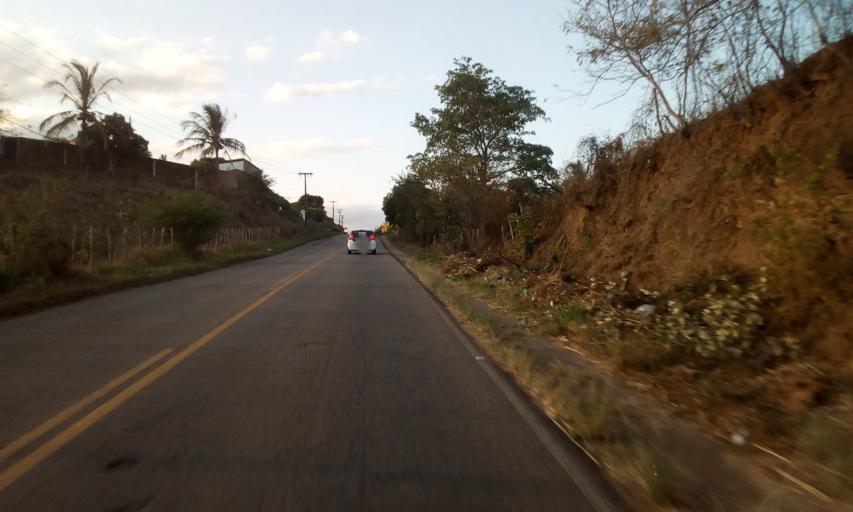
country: BR
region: Paraiba
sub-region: Guarabira
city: Guarabira
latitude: -6.9075
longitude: -35.4552
